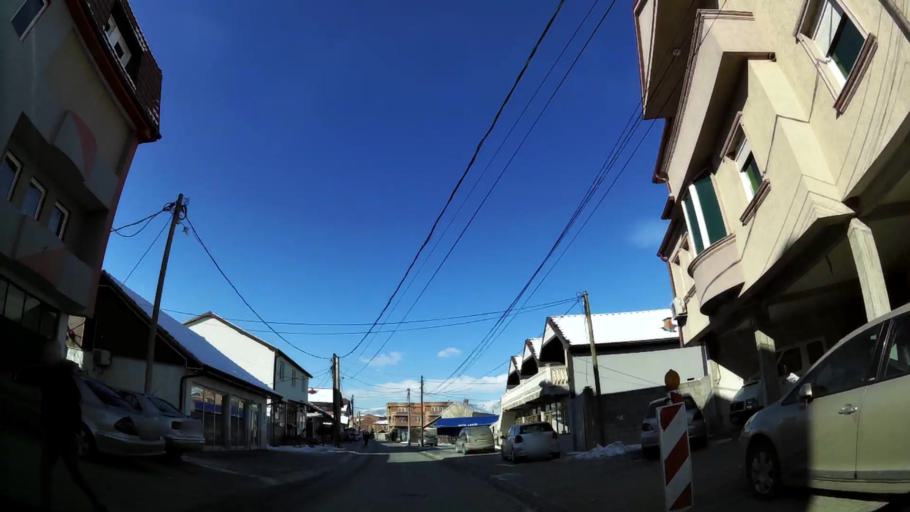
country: MK
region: Saraj
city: Saraj
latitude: 42.0003
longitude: 21.3265
